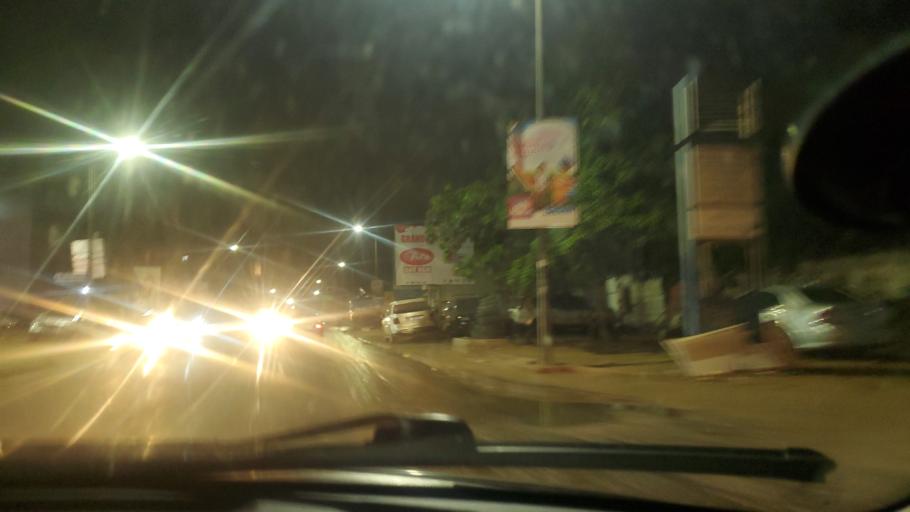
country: SN
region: Dakar
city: Grand Dakar
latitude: 14.7235
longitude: -17.4461
